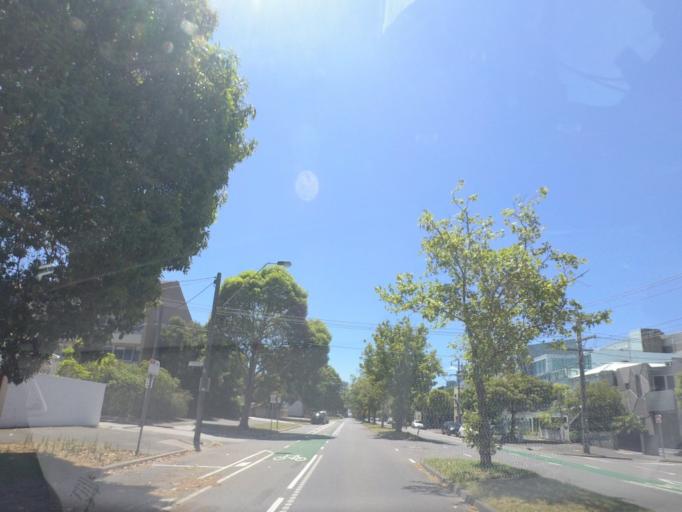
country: AU
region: Victoria
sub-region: Port Phillip
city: South Melbourne
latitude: -37.8374
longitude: 144.9655
